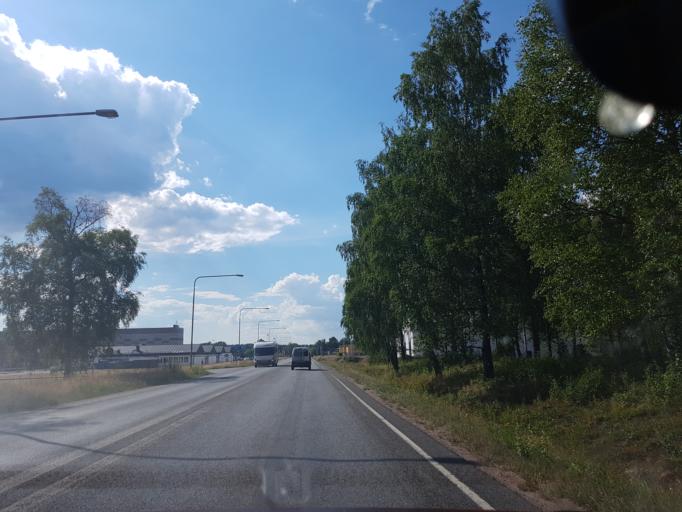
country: SE
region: Joenkoeping
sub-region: Gislaveds Kommun
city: Gislaved
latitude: 57.2955
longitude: 13.5701
